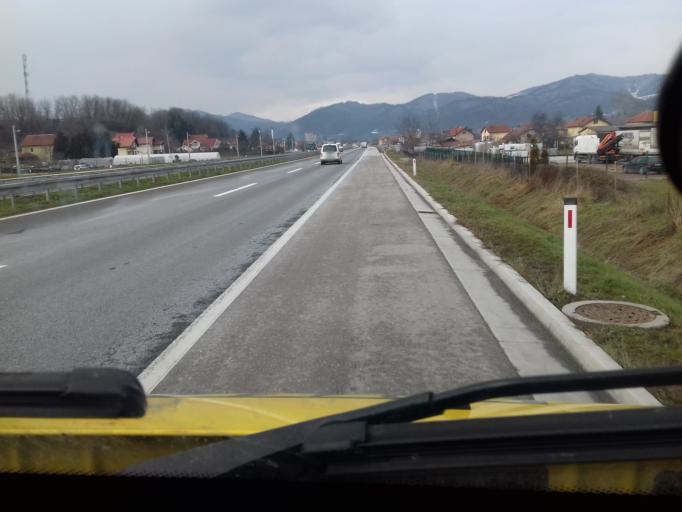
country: BA
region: Federation of Bosnia and Herzegovina
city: Gornje Mostre
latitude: 44.0185
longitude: 18.1369
